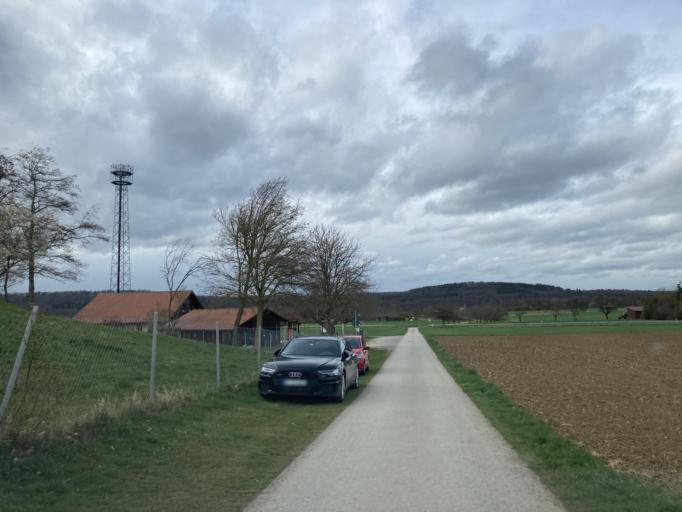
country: DE
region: Baden-Wuerttemberg
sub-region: Tuebingen Region
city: Kirchentellinsfurt
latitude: 48.5330
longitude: 9.1612
